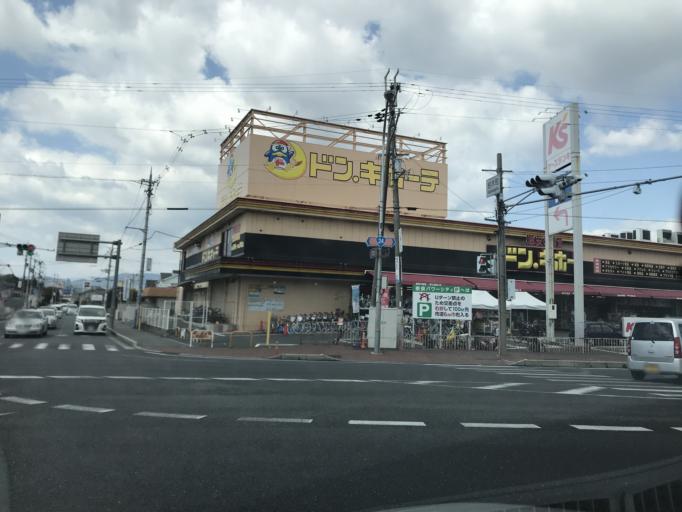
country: JP
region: Nara
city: Nara-shi
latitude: 34.6700
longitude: 135.8000
